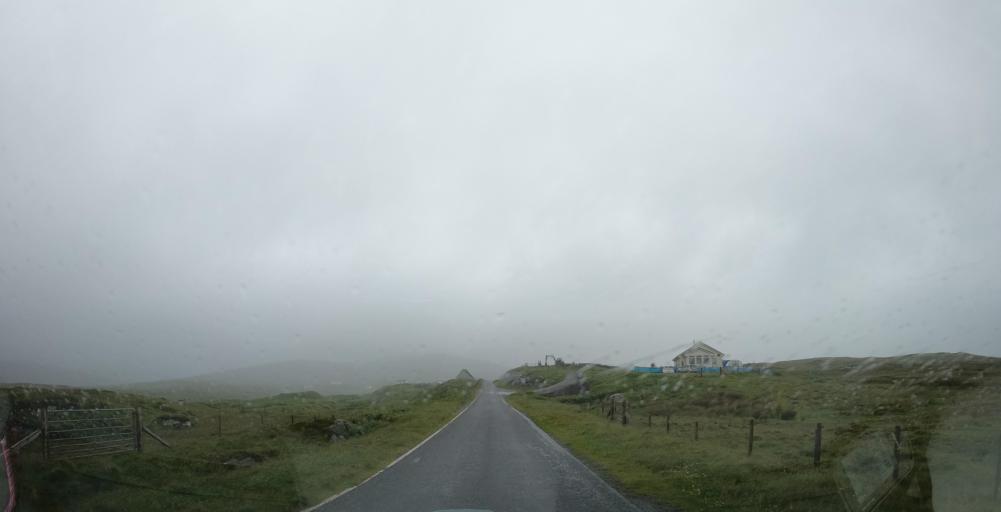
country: GB
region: Scotland
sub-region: Eilean Siar
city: Barra
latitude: 57.0079
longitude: -7.4131
